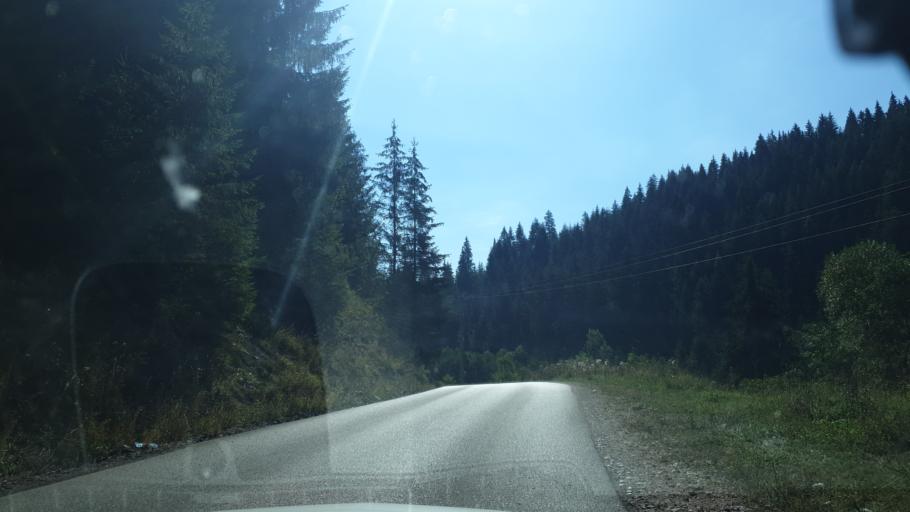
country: RS
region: Central Serbia
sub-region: Zlatiborski Okrug
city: Nova Varos
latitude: 43.4506
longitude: 19.8446
